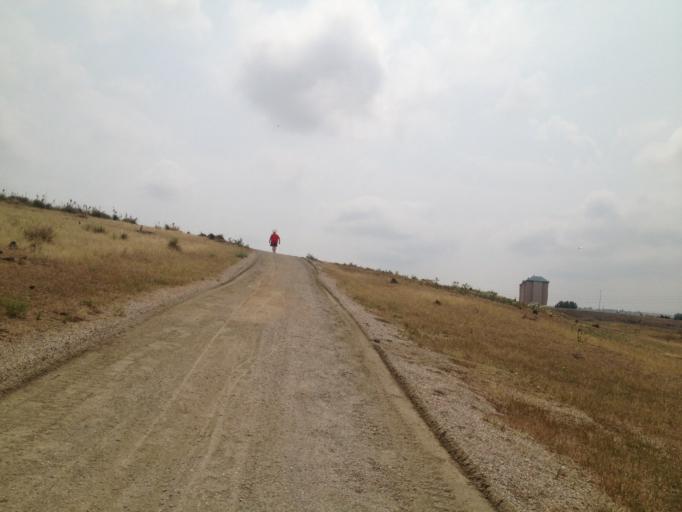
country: US
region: Colorado
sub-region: Broomfield County
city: Broomfield
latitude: 39.9323
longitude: -105.1125
